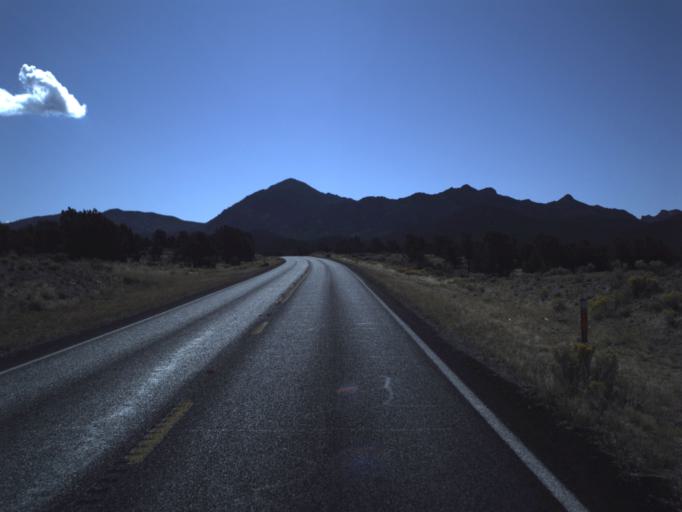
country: US
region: Utah
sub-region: Washington County
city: Enterprise
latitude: 37.6182
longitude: -113.4121
